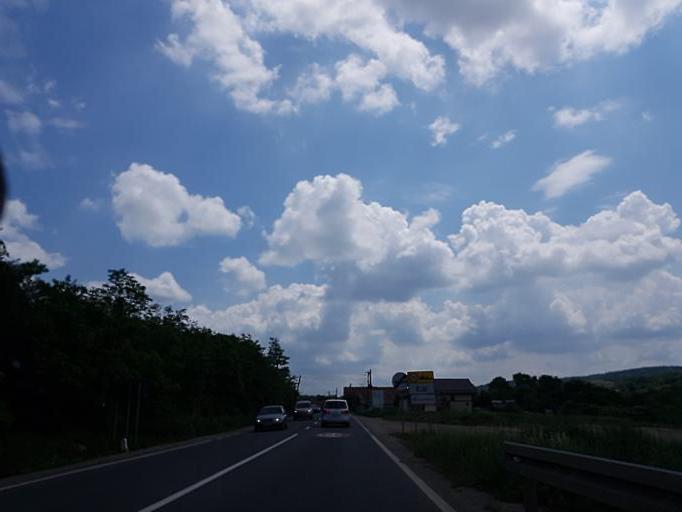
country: RO
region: Sibiu
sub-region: Comuna Seica Mare
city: Seica Mare
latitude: 45.9671
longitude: 24.1576
